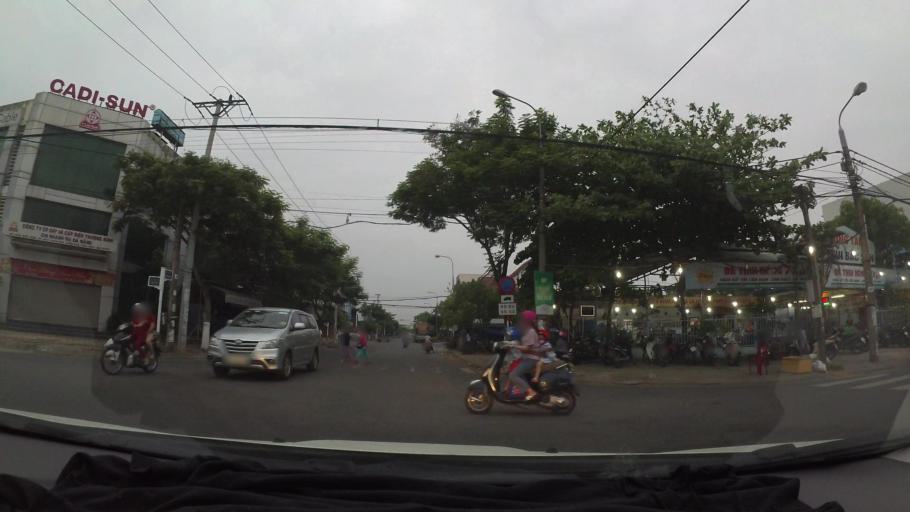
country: VN
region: Da Nang
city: Thanh Khe
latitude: 16.0563
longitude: 108.1762
